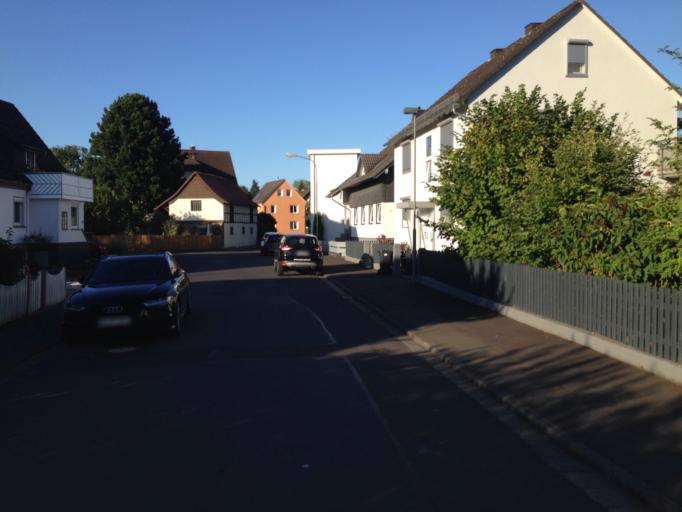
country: DE
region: Hesse
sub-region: Regierungsbezirk Giessen
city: Lich
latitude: 50.5481
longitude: 8.7802
